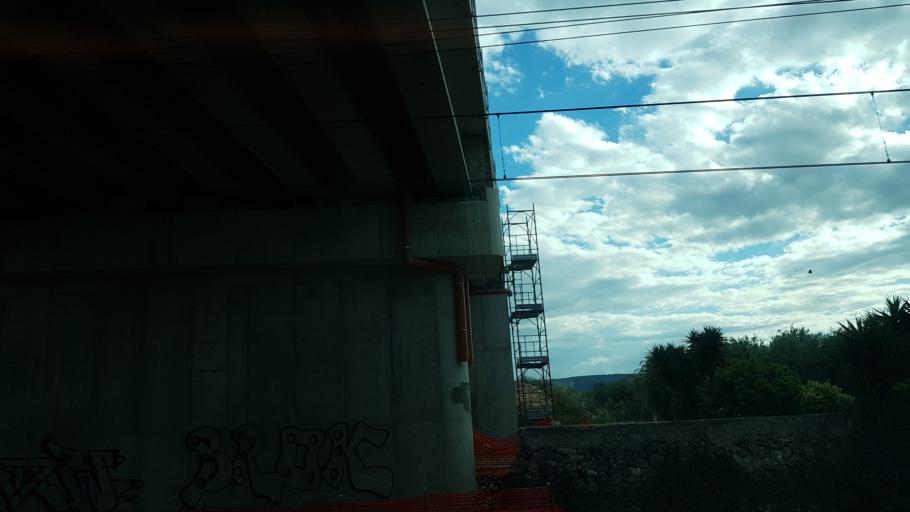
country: IT
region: Apulia
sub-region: Provincia di Brindisi
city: Montalbano
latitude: 40.8159
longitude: 17.4585
